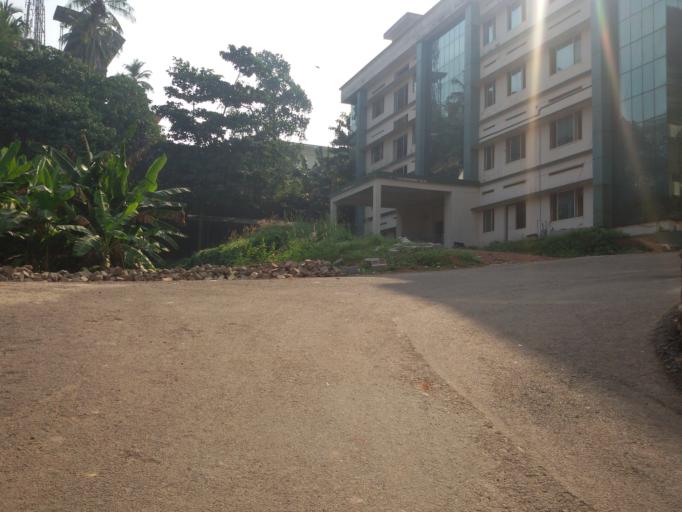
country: IN
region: Kerala
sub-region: Kozhikode
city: Kunnamangalam
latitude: 11.2941
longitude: 75.8228
